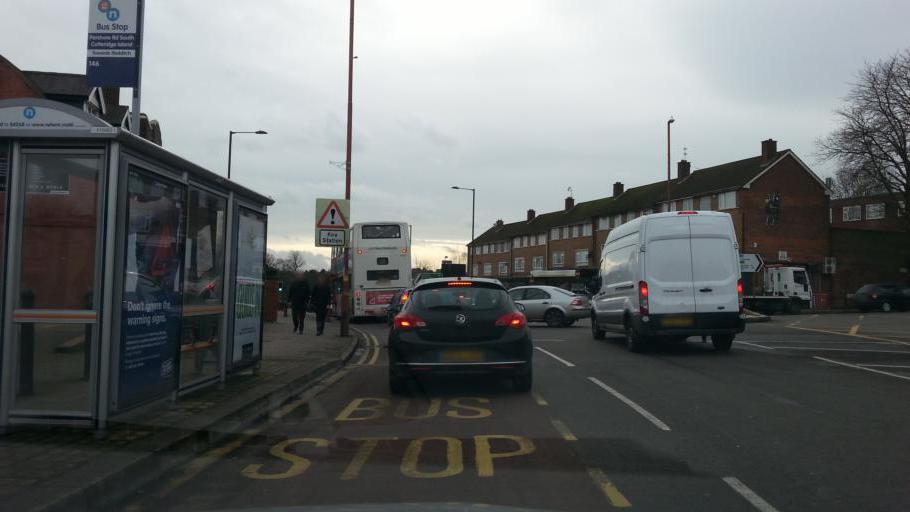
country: GB
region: England
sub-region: City and Borough of Birmingham
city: Bartley Green
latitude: 52.4157
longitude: -1.9307
